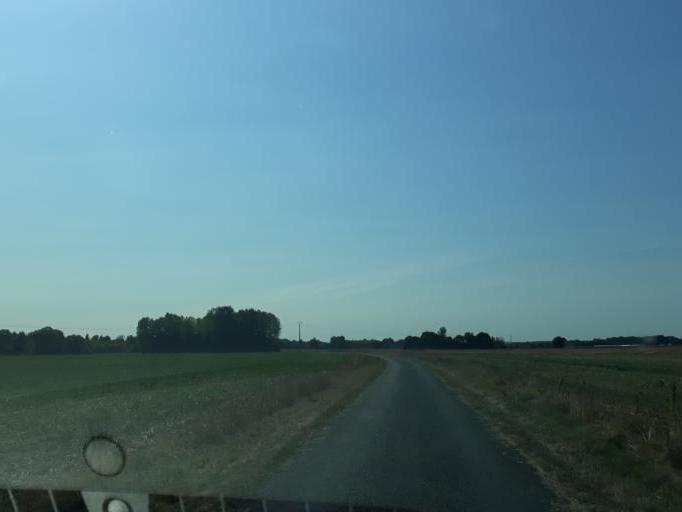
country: FR
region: Centre
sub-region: Departement du Loir-et-Cher
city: Selles-sur-Cher
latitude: 47.2673
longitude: 1.5975
